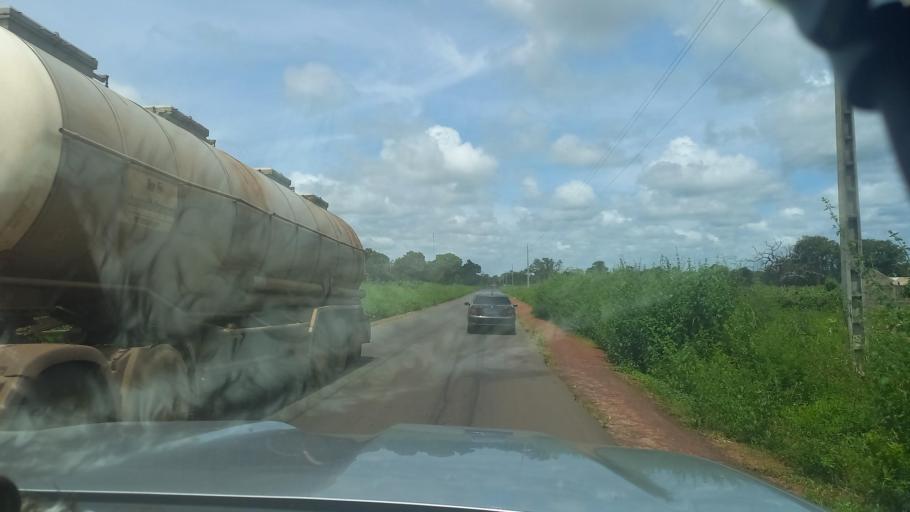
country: GM
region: Lower River
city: Kaiaf
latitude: 13.2001
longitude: -15.5515
